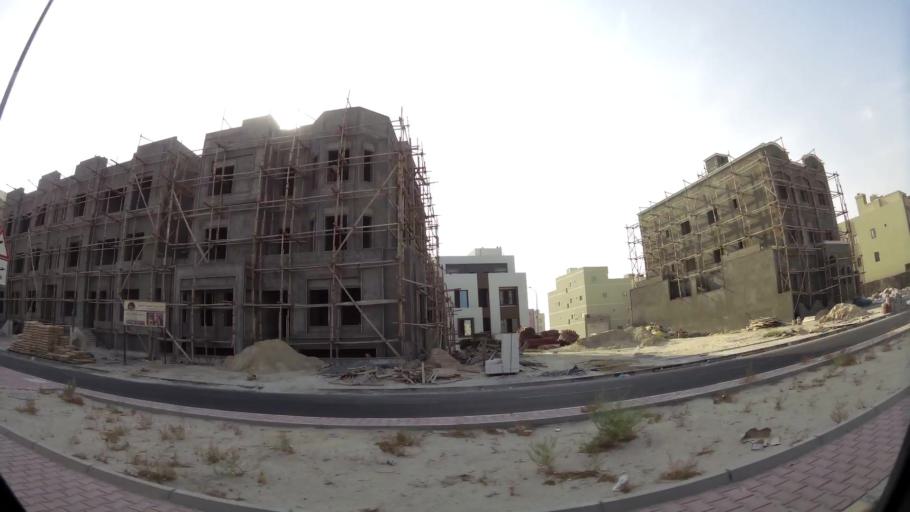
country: KW
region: Mubarak al Kabir
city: Mubarak al Kabir
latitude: 29.1890
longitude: 48.1064
